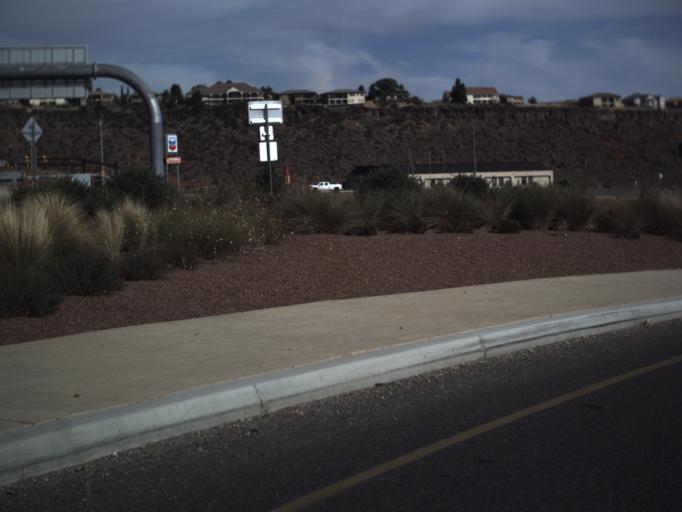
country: US
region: Utah
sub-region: Washington County
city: Saint George
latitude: 37.1096
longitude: -113.5595
